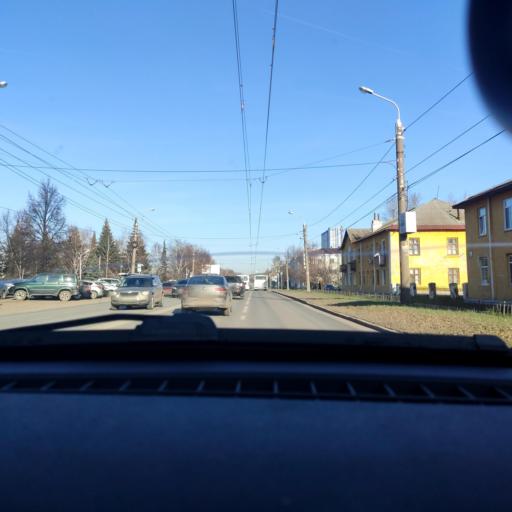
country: RU
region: Bashkortostan
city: Ufa
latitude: 54.7918
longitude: 56.1393
